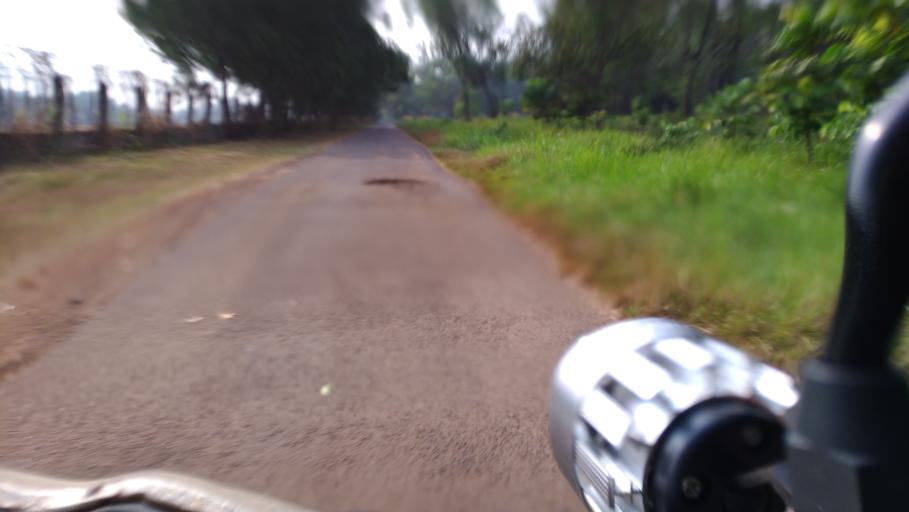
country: ID
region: West Java
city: Cileungsir
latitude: -6.3569
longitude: 106.9010
